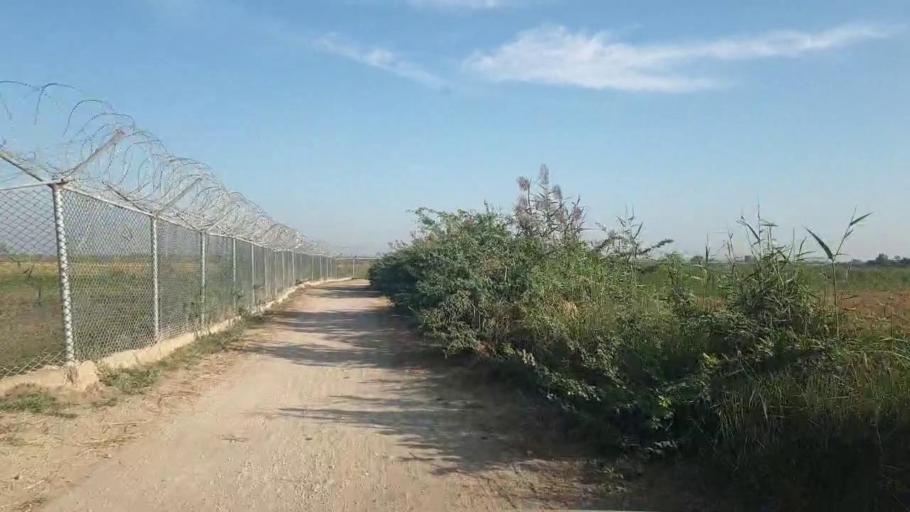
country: PK
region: Sindh
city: Talhar
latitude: 24.8418
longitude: 68.8542
